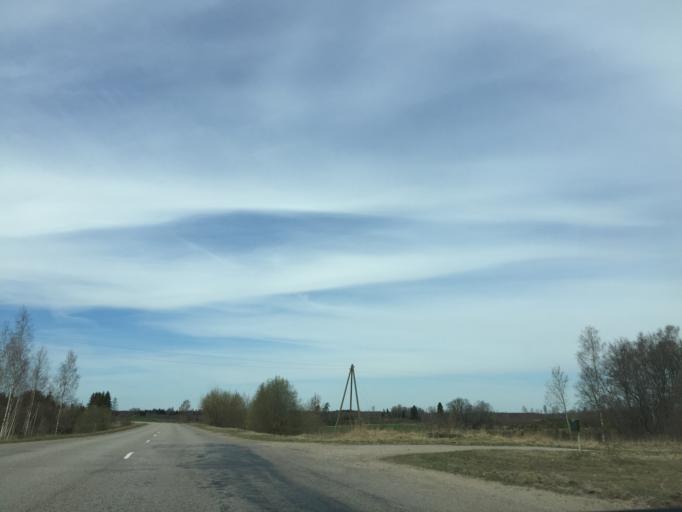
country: LV
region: Valkas Rajons
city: Valka
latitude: 57.7863
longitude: 25.9013
